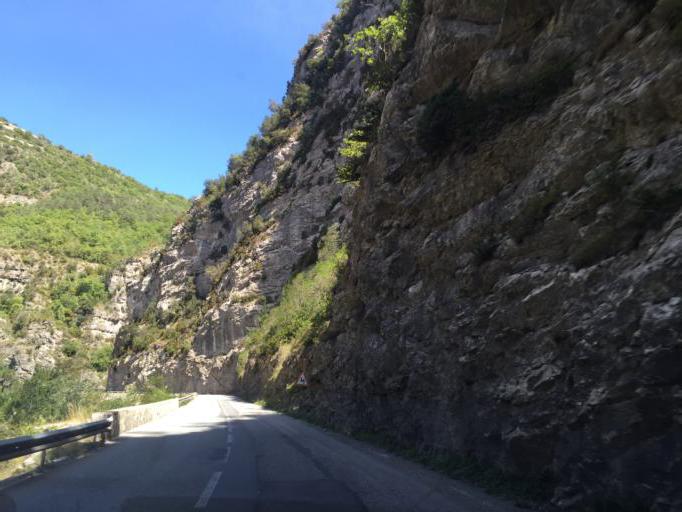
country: FR
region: Provence-Alpes-Cote d'Azur
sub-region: Departement des Alpes-Maritimes
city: Gilette
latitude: 43.9370
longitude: 7.1679
